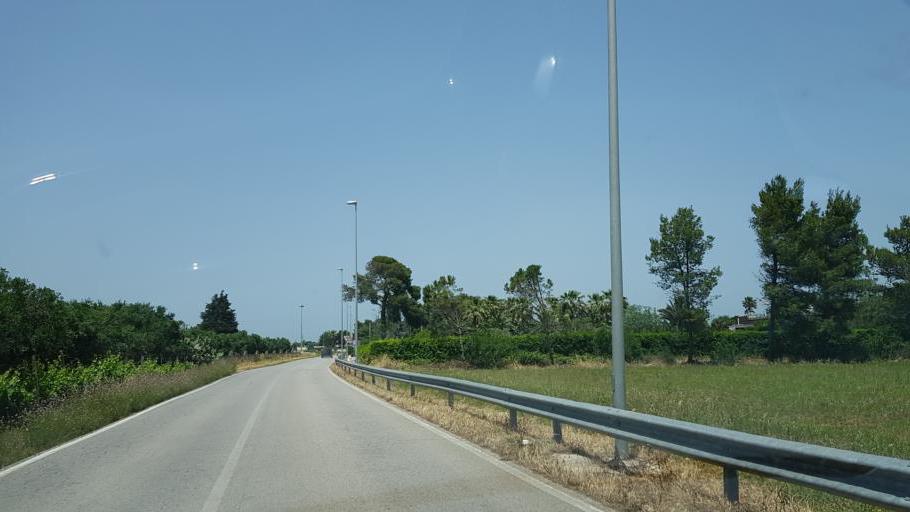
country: IT
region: Apulia
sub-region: Provincia di Brindisi
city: Mesagne
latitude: 40.5395
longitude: 17.8171
